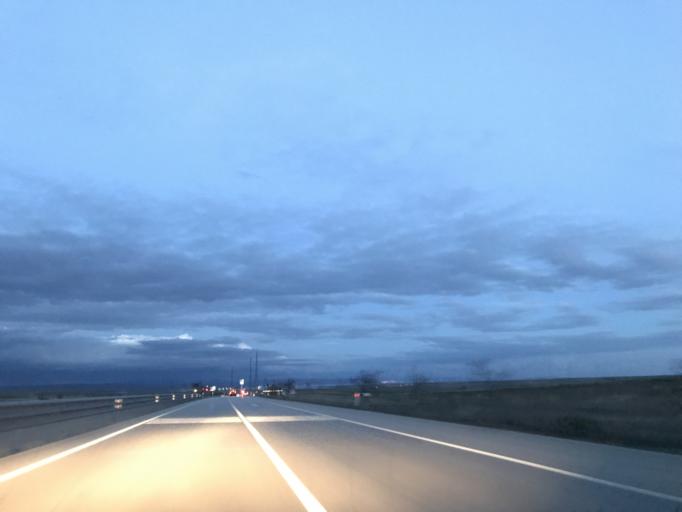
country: TR
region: Konya
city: Kulu
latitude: 39.1601
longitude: 33.1971
